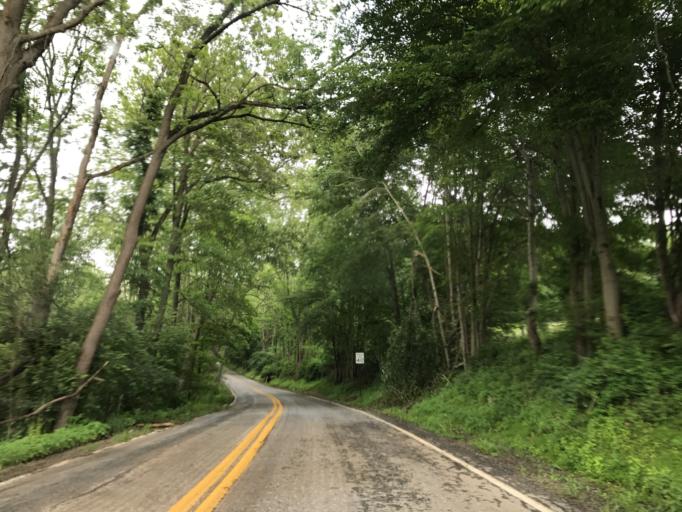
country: US
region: Pennsylvania
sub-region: York County
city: Susquehanna Trails
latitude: 39.7782
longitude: -76.4201
